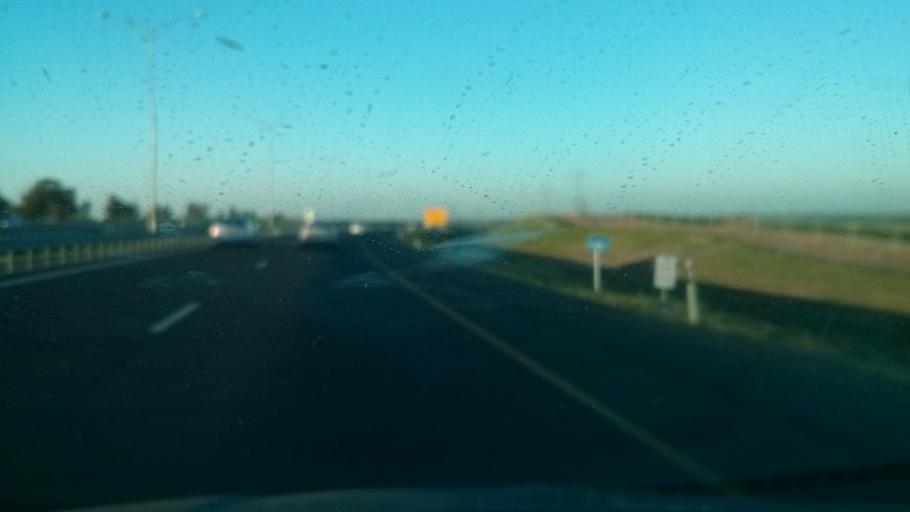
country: IL
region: Southern District
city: Lehavim
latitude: 31.4575
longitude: 34.7697
